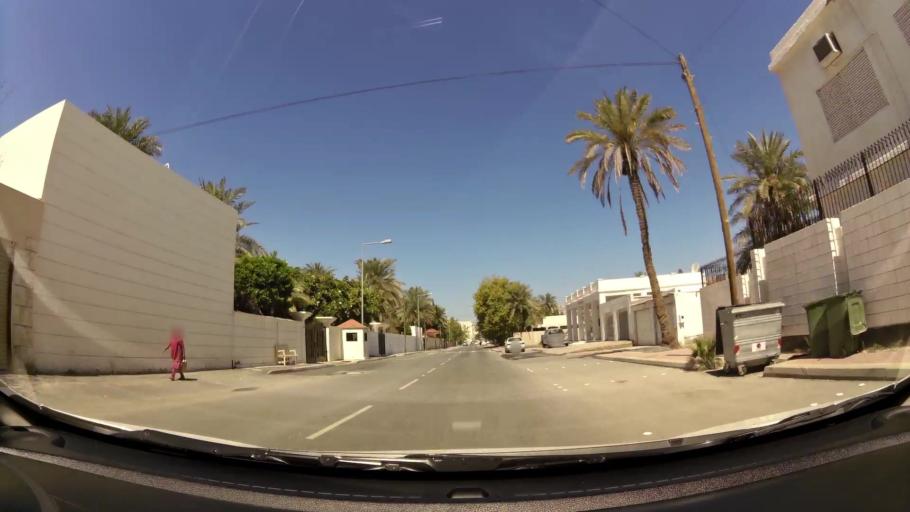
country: BH
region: Muharraq
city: Al Muharraq
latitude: 26.2622
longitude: 50.6081
